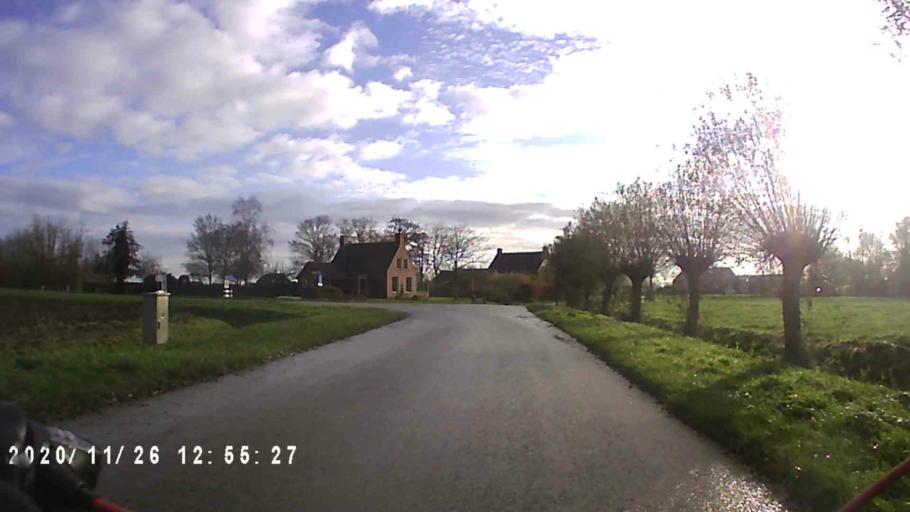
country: NL
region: Groningen
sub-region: Gemeente Appingedam
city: Appingedam
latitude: 53.3478
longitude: 6.7993
